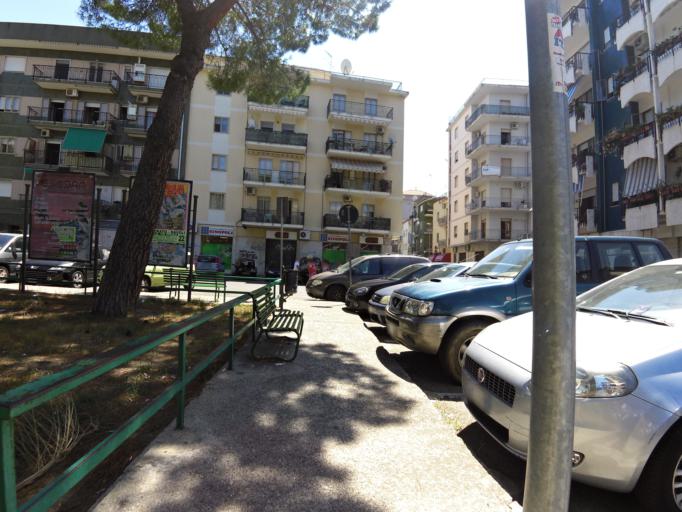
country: IT
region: Calabria
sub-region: Provincia di Catanzaro
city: Soverato Marina
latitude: 38.6885
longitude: 16.5512
